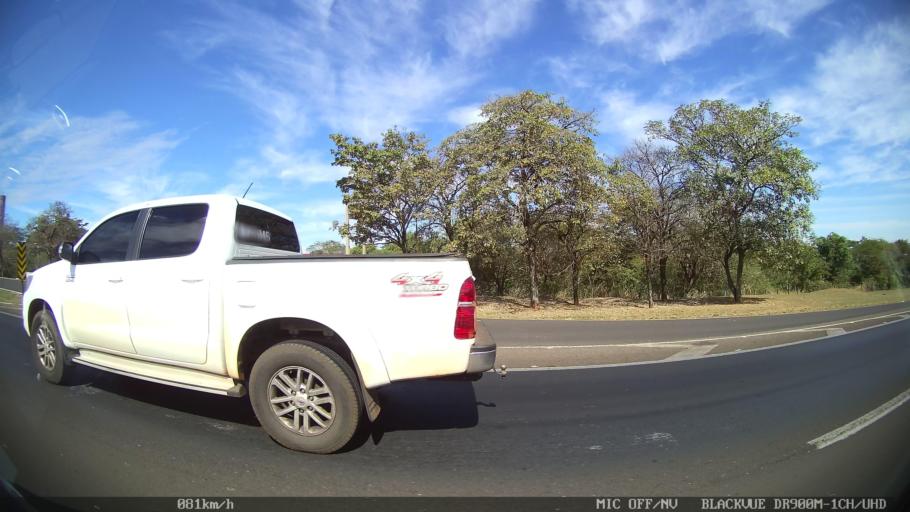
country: BR
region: Sao Paulo
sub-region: Sao Jose Do Rio Preto
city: Sao Jose do Rio Preto
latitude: -20.8220
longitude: -49.4252
